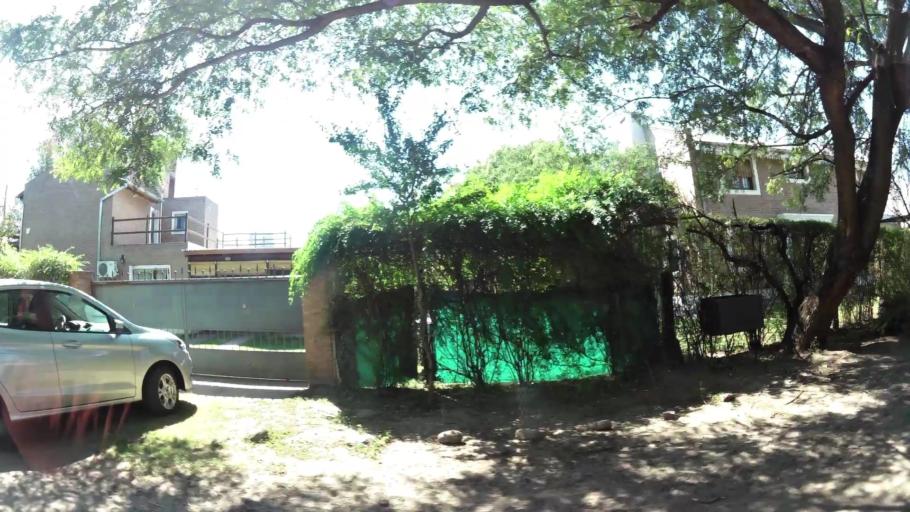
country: AR
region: Cordoba
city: Villa Allende
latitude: -31.2969
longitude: -64.2820
